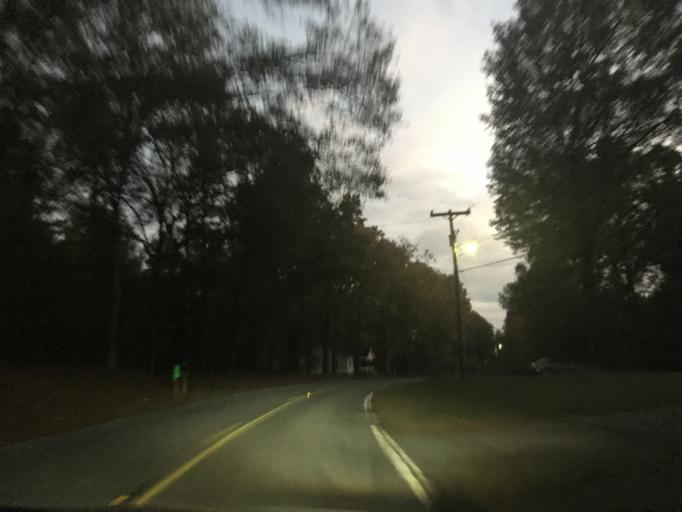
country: US
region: South Carolina
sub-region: Spartanburg County
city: Mayo
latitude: 35.0529
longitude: -81.8906
